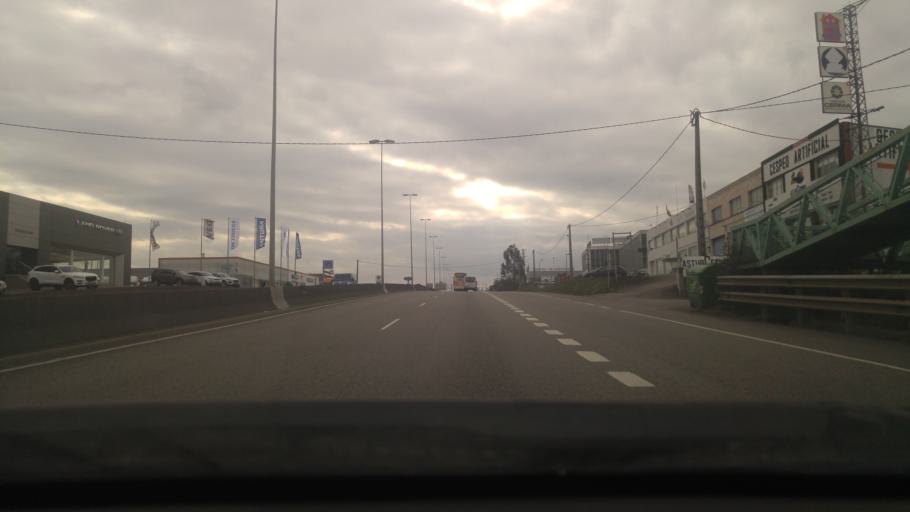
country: ES
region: Asturias
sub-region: Province of Asturias
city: Natahoyo
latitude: 43.5067
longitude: -5.6967
